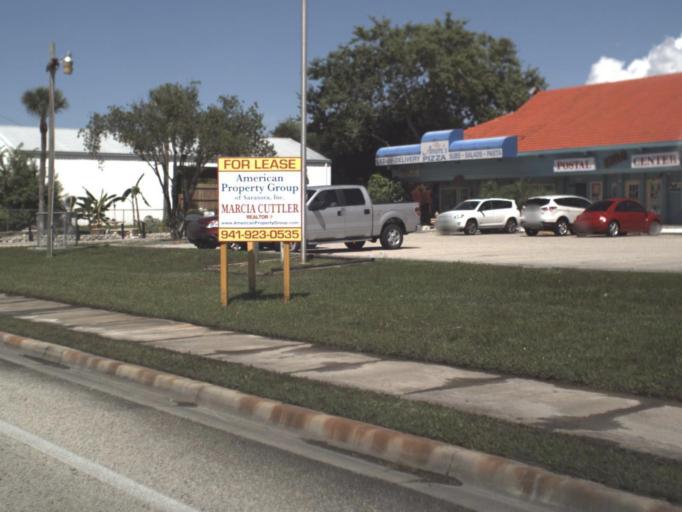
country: US
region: Florida
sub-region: Sarasota County
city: South Venice
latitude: 27.0504
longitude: -82.4067
